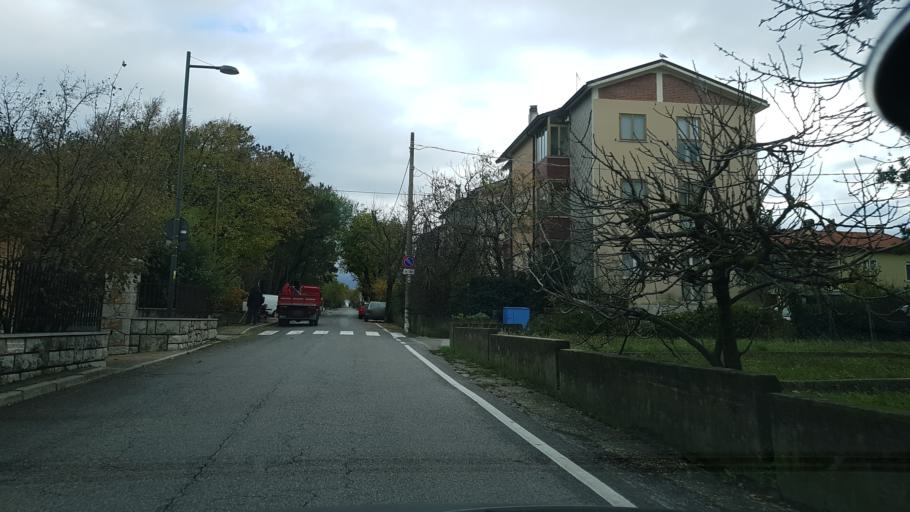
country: IT
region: Friuli Venezia Giulia
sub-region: Provincia di Trieste
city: Prosecco-Contovello
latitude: 45.7013
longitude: 13.7388
